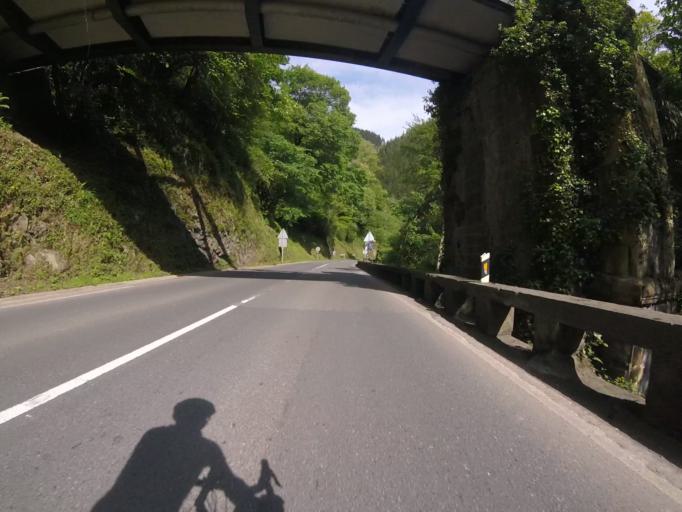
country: ES
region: Basque Country
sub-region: Provincia de Guipuzcoa
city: Azkoitia
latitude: 43.1541
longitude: -2.3413
